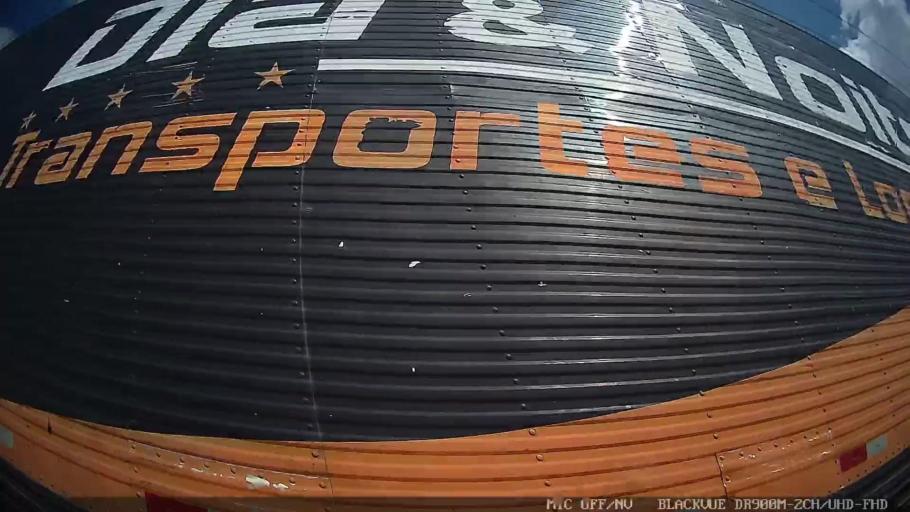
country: BR
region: Sao Paulo
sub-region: Guarulhos
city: Guarulhos
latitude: -23.5134
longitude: -46.5048
